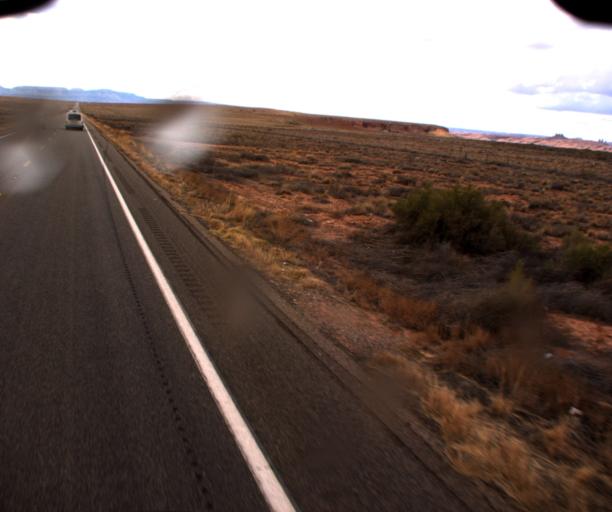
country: US
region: Arizona
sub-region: Navajo County
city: Kayenta
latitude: 36.7557
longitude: -110.0529
